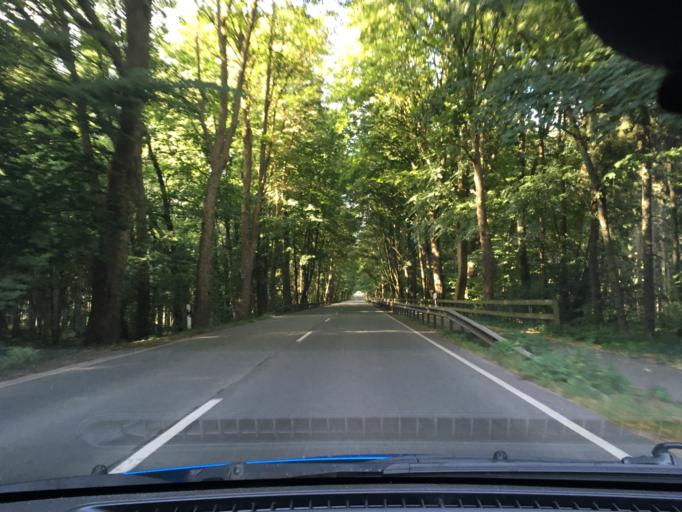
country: DE
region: Lower Saxony
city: Seevetal
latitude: 53.4157
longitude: 9.9281
